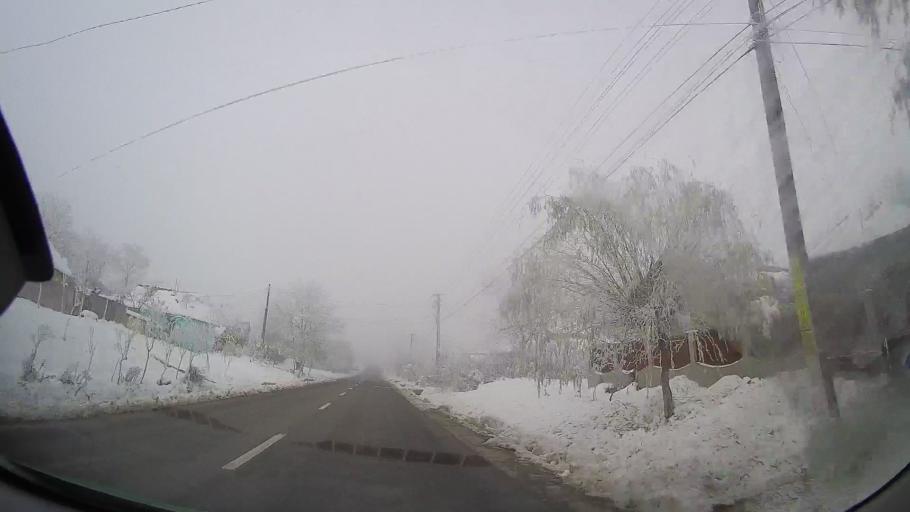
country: RO
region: Iasi
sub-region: Comuna Halaucesti
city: Halaucesti
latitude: 47.0996
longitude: 26.8173
